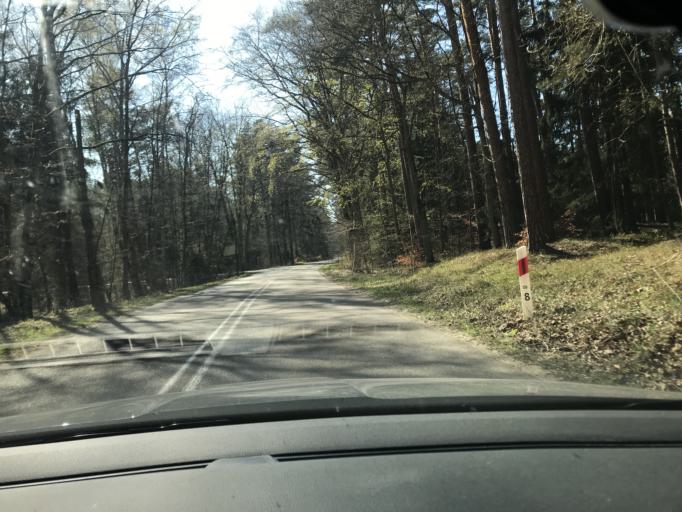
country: PL
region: Pomeranian Voivodeship
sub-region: Powiat nowodworski
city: Krynica Morska
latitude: 54.3609
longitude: 19.3530
